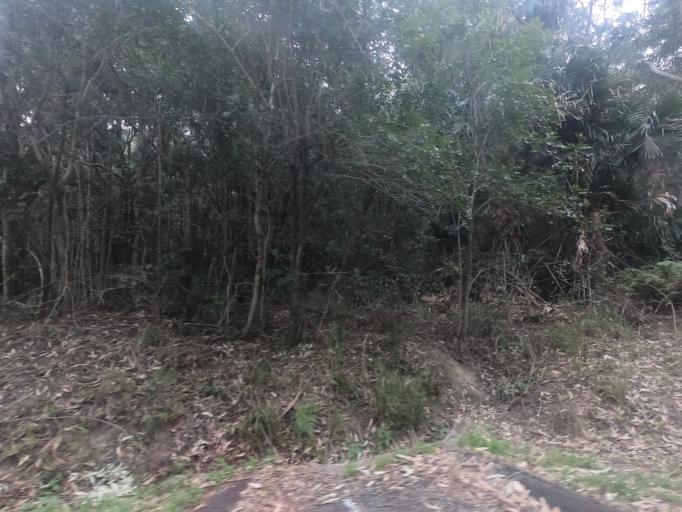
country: AU
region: New South Wales
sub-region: Wollongong
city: Bulli
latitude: -34.2959
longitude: 150.9347
